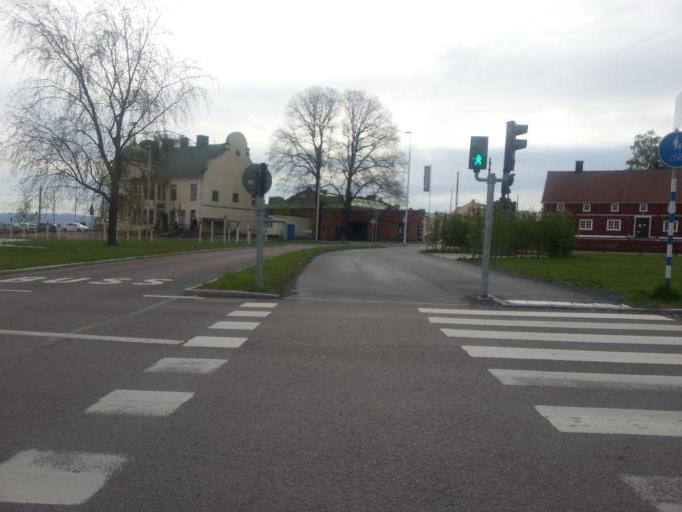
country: SE
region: Joenkoeping
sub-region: Jonkopings Kommun
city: Jonkoping
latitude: 57.7856
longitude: 14.1543
